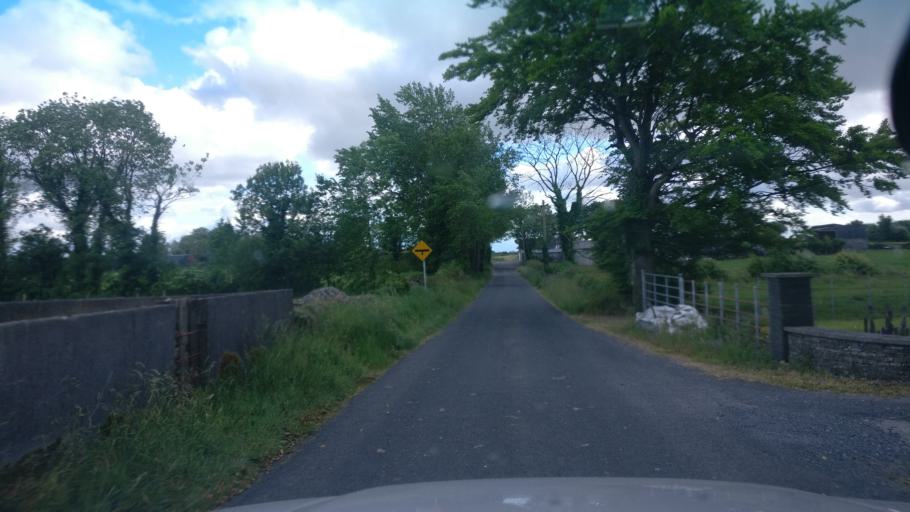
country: IE
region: Connaught
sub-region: County Galway
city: Portumna
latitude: 53.1799
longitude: -8.3404
